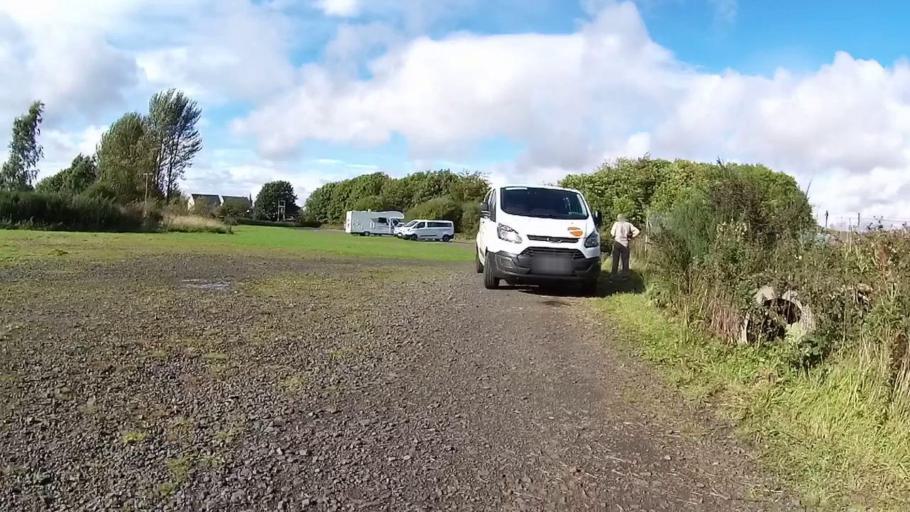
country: GB
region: Scotland
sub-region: Perth and Kinross
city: Kinross
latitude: 56.1993
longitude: -3.4175
